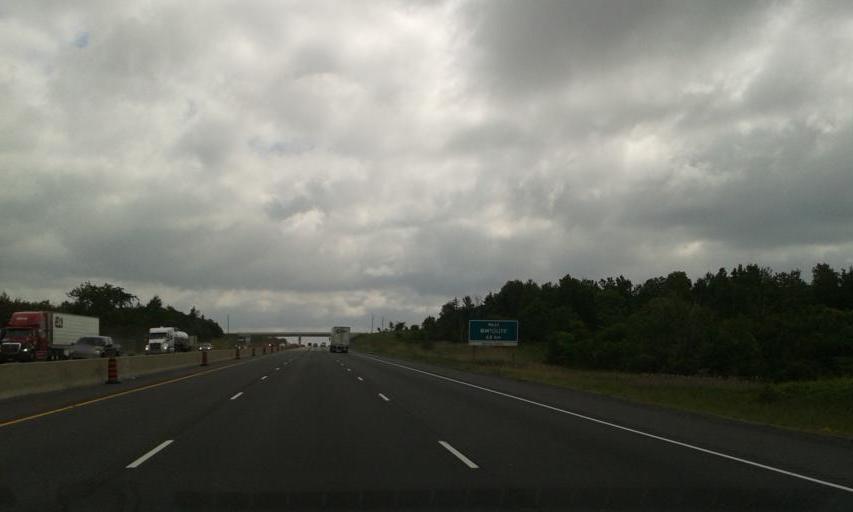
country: CA
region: Ontario
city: Cobourg
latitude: 43.9383
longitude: -78.4563
